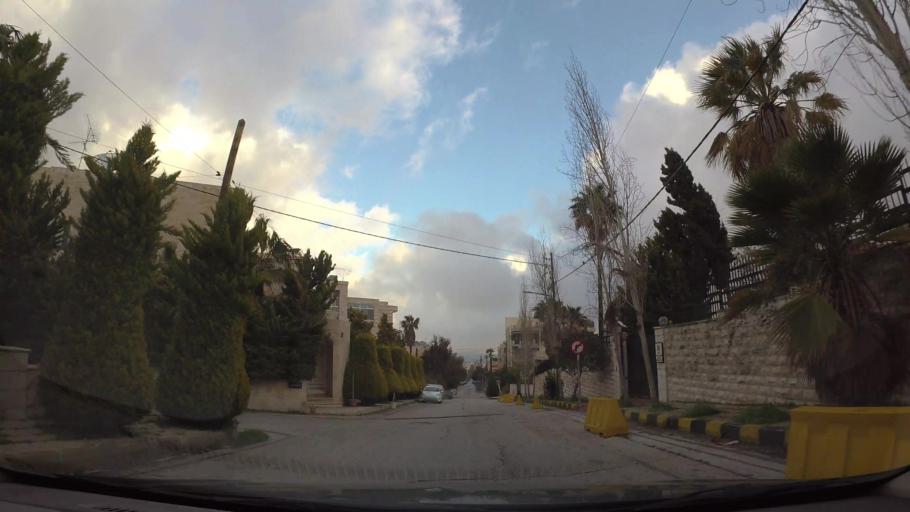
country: JO
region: Amman
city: Amman
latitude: 31.9566
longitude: 35.8860
